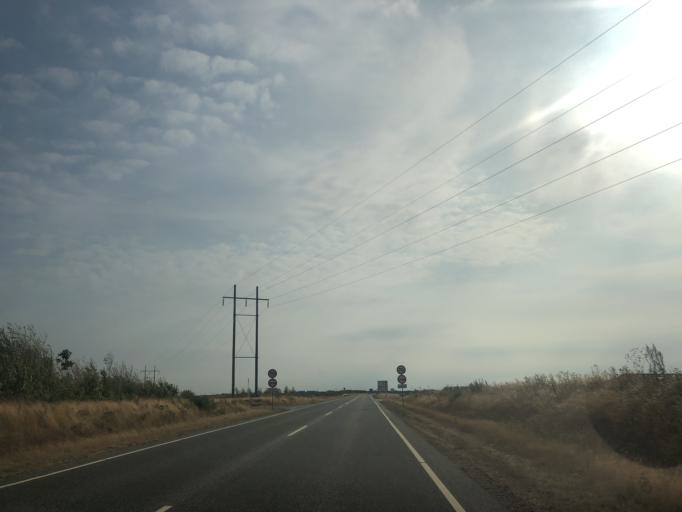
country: DK
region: Central Jutland
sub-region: Skive Kommune
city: Skive
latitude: 56.6765
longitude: 8.9633
